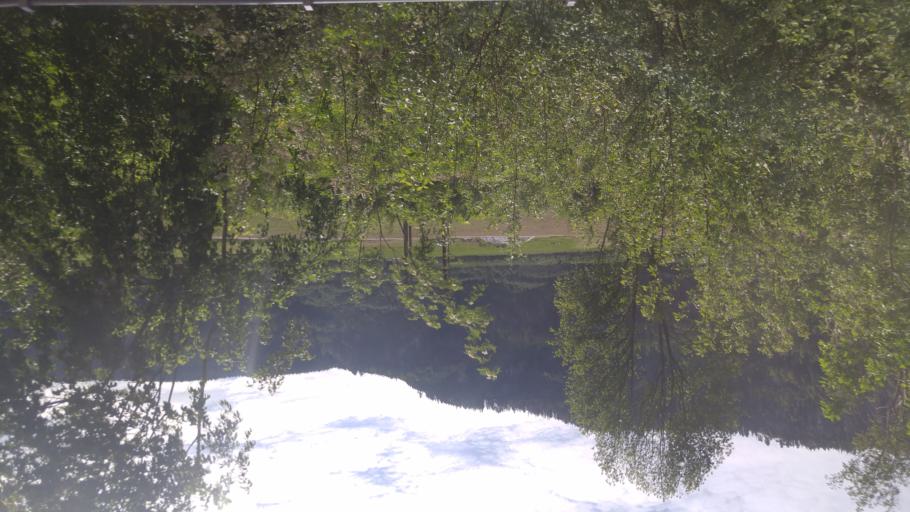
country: NO
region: Sor-Trondelag
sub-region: Midtre Gauldal
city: Storen
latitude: 63.0495
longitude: 10.2845
